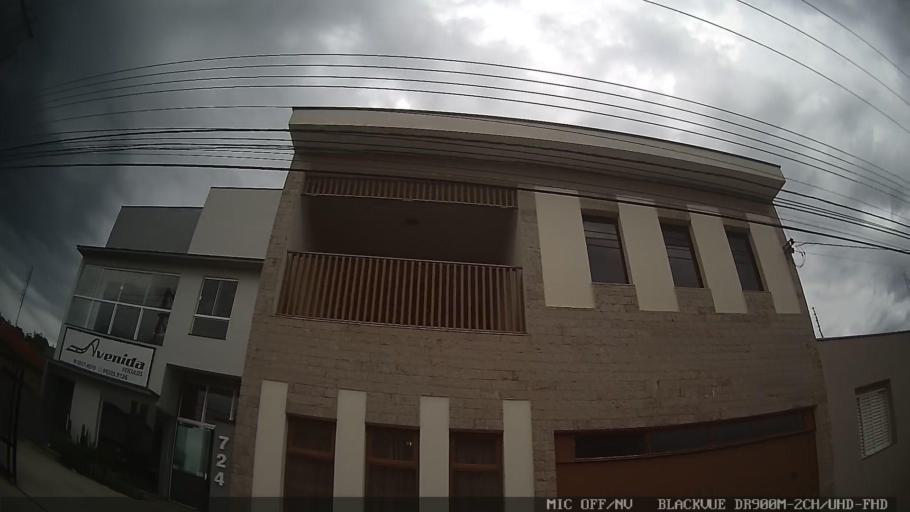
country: BR
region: Sao Paulo
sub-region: Amparo
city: Amparo
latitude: -22.7063
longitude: -46.7775
